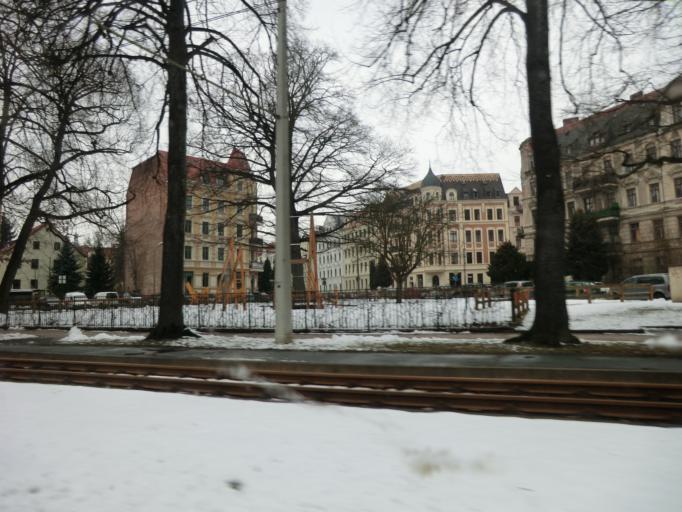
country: DE
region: Saxony
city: Goerlitz
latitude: 51.1430
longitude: 14.9706
